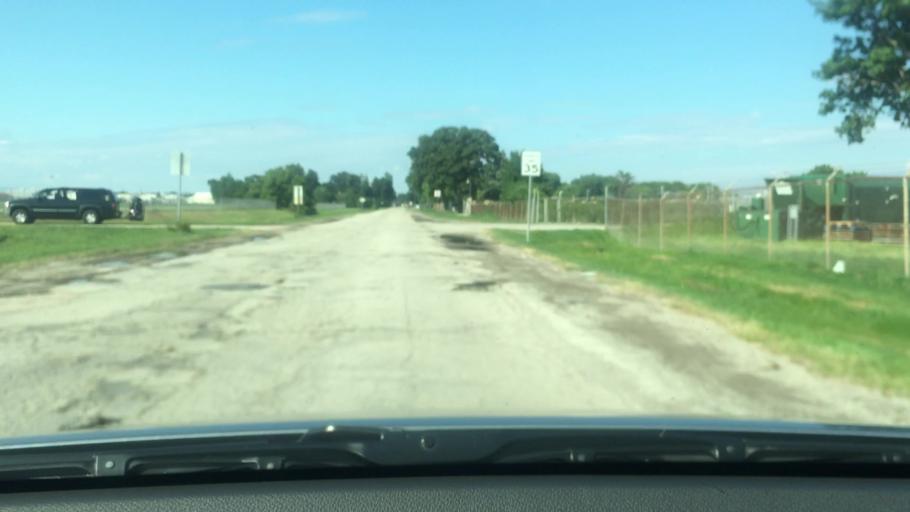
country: US
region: Wisconsin
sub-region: Winnebago County
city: Oshkosh
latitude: 43.9822
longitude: -88.5524
